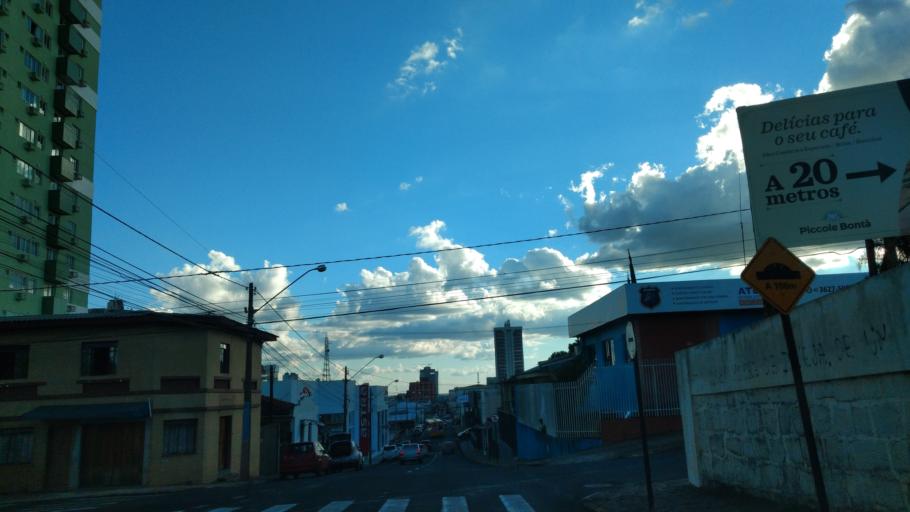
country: BR
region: Parana
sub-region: Guarapuava
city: Guarapuava
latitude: -25.3880
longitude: -51.4635
